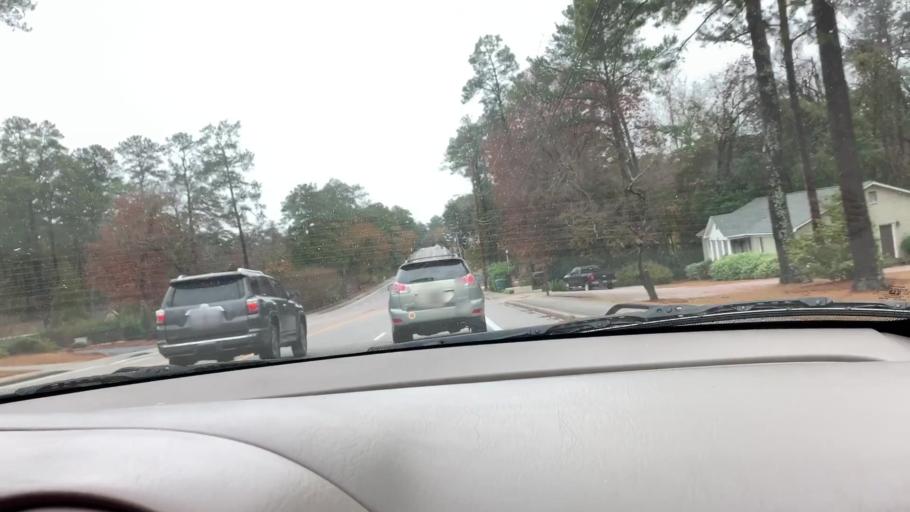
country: US
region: South Carolina
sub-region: Richland County
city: Dentsville
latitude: 34.0358
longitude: -80.9644
